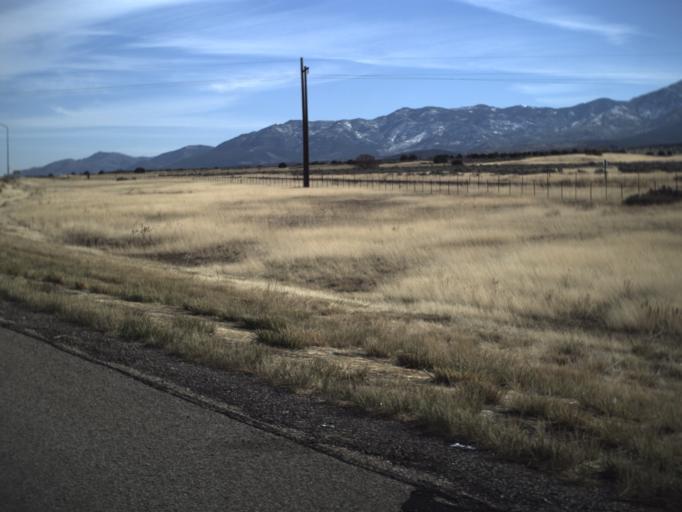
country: US
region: Utah
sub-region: Millard County
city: Fillmore
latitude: 38.9931
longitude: -112.3218
